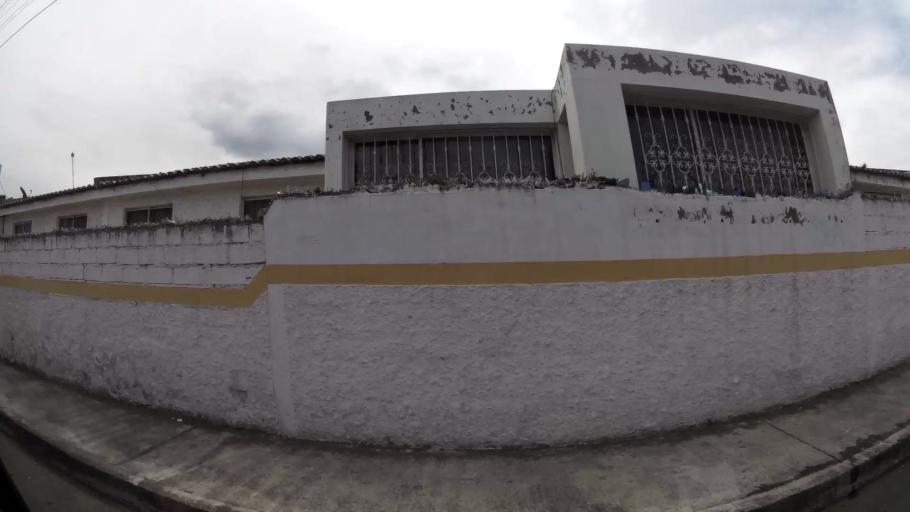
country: EC
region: Cotopaxi
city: Latacunga
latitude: -0.9259
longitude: -78.6131
